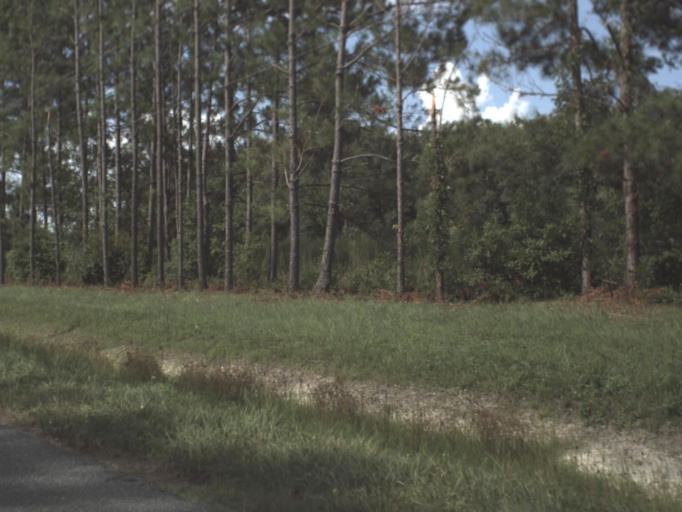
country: US
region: Florida
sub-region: Taylor County
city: Perry
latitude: 30.2461
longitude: -83.6213
